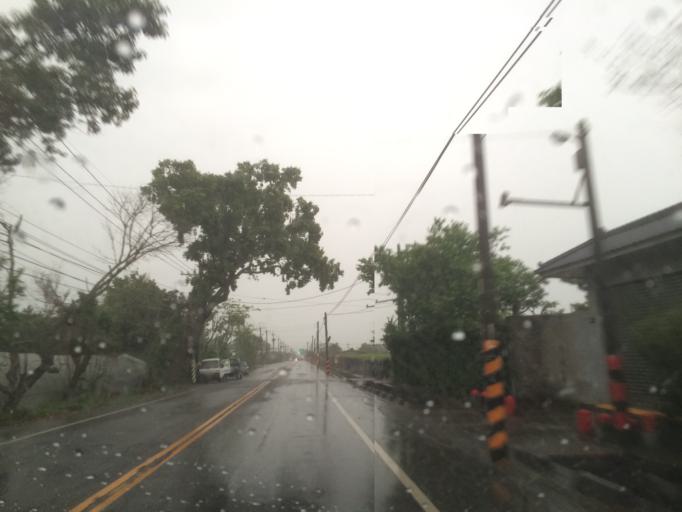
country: TW
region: Taiwan
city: Fengyuan
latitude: 24.2159
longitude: 120.8033
